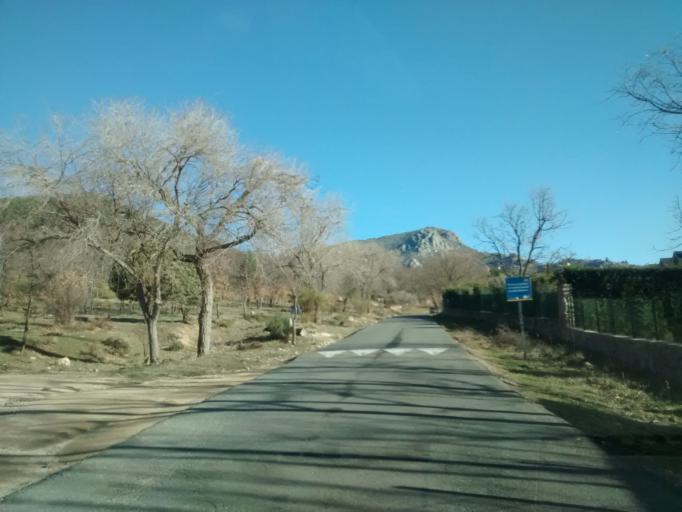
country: ES
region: Madrid
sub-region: Provincia de Madrid
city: Navacerrada
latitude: 40.7381
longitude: -4.0088
